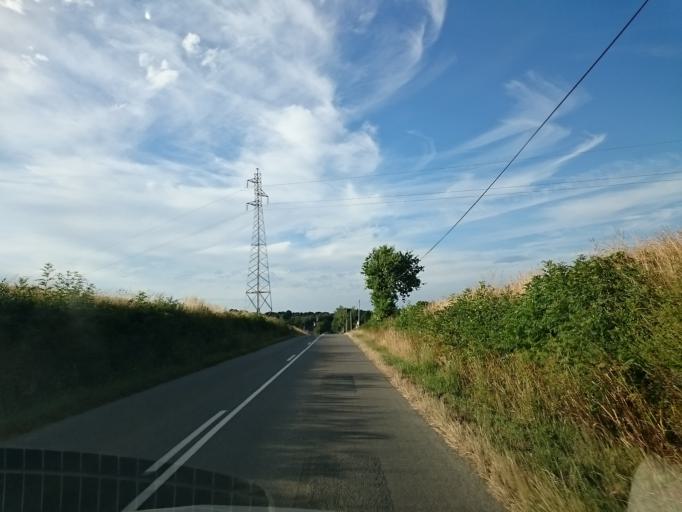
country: FR
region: Brittany
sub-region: Departement d'Ille-et-Vilaine
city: Chanteloup
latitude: 47.9230
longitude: -1.6177
